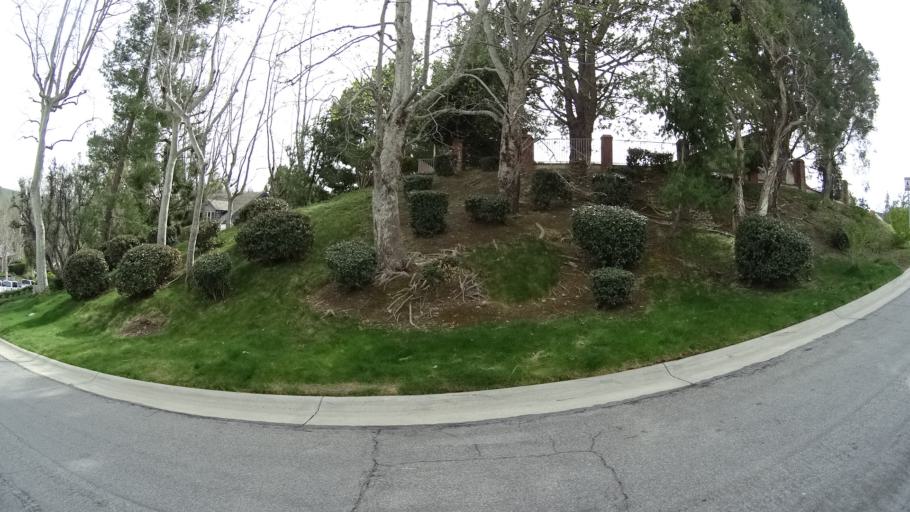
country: US
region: California
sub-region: Orange County
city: Villa Park
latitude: 33.8343
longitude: -117.7465
